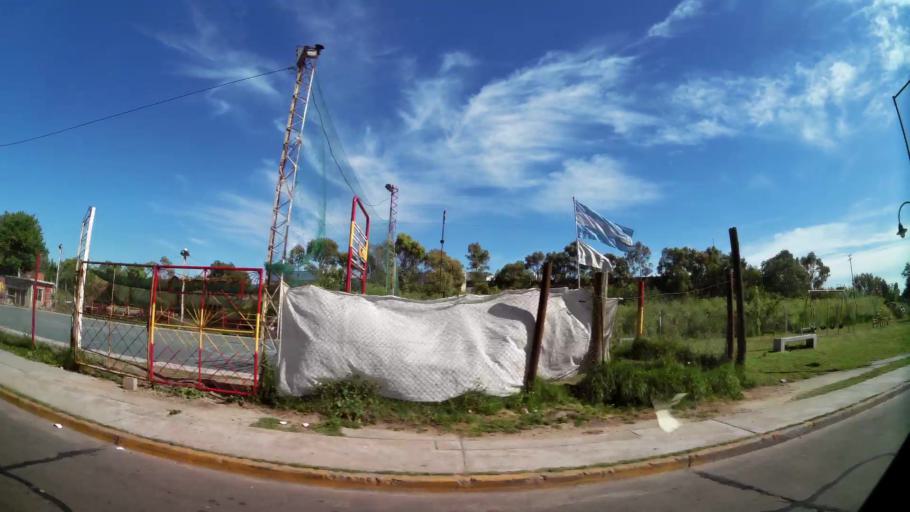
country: AR
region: Buenos Aires
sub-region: Partido de Tigre
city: Tigre
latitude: -34.4746
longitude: -58.5790
